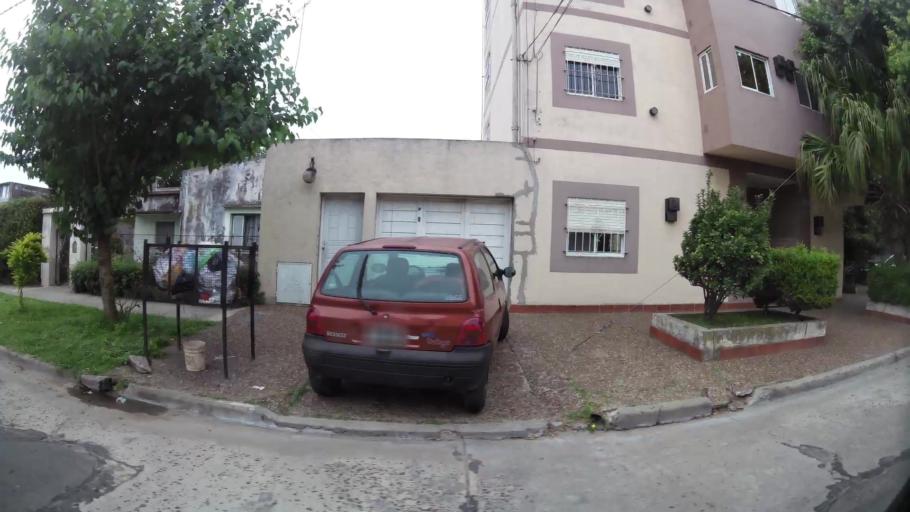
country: AR
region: Buenos Aires
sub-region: Partido de Campana
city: Campana
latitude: -34.1718
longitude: -58.9577
